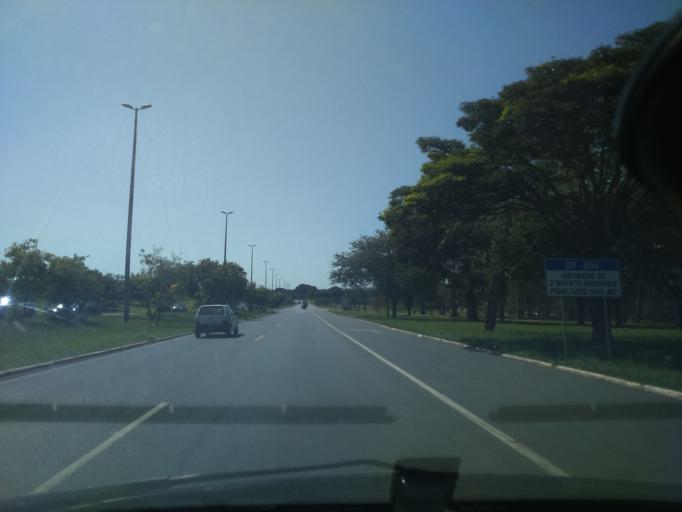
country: BR
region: Federal District
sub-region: Brasilia
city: Brasilia
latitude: -15.8454
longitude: -47.9287
